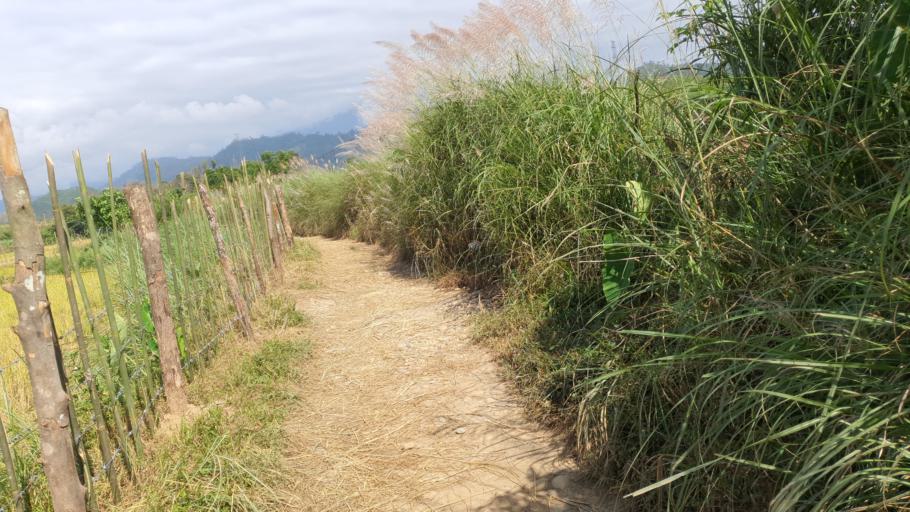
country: LA
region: Bolikhamxai
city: Bolikhan
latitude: 18.9082
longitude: 103.7426
